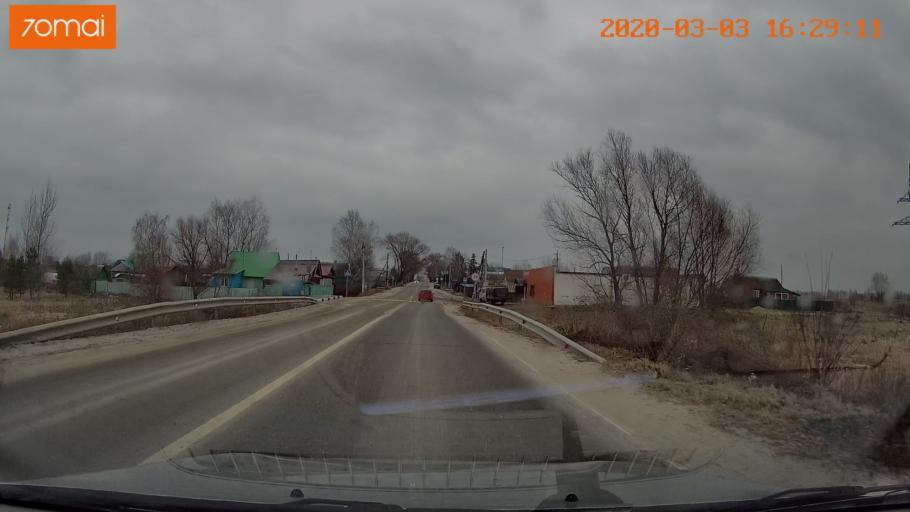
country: RU
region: Moskovskaya
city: Konobeyevo
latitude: 55.4374
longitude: 38.6982
